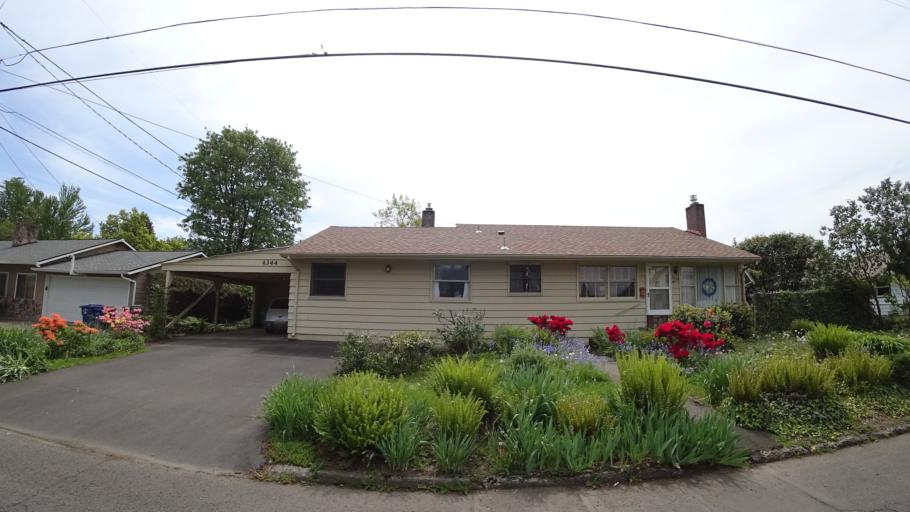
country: US
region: Oregon
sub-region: Clackamas County
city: Milwaukie
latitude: 45.4528
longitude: -122.6178
